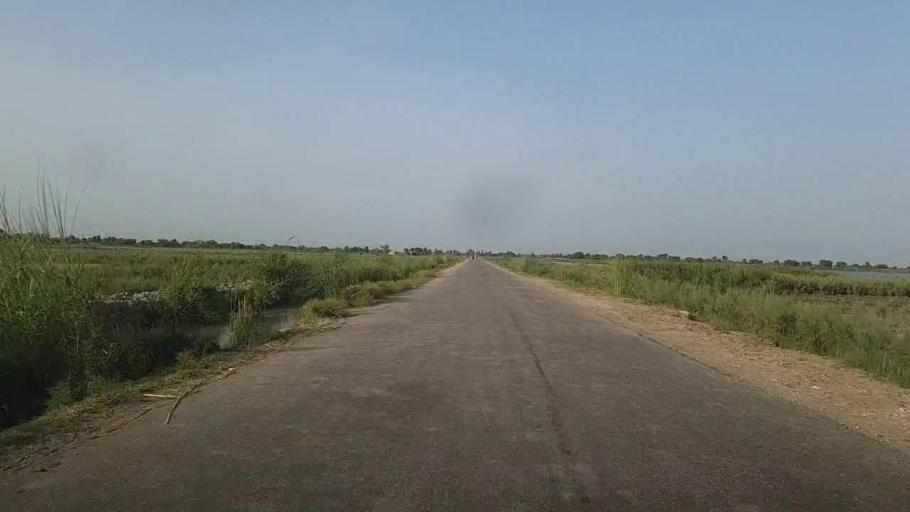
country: PK
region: Sindh
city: Ubauro
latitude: 28.0906
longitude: 69.8039
